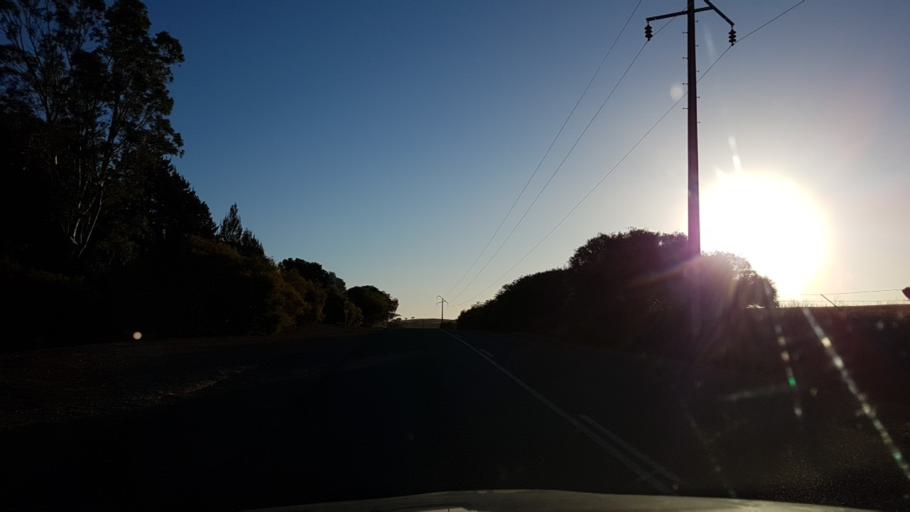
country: AU
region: South Australia
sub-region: Clare and Gilbert Valleys
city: Clare
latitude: -34.0211
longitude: 138.6985
